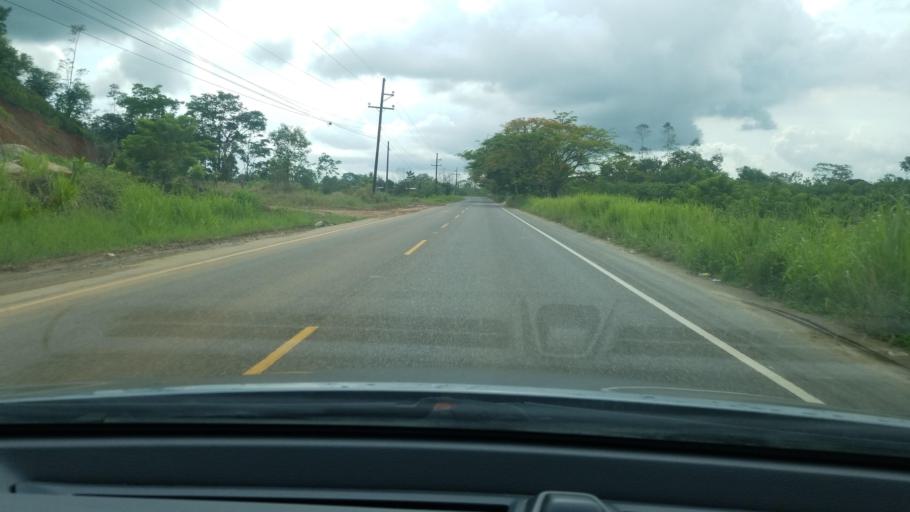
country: HN
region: Cortes
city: Potrerillos
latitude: 15.5954
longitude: -88.3151
